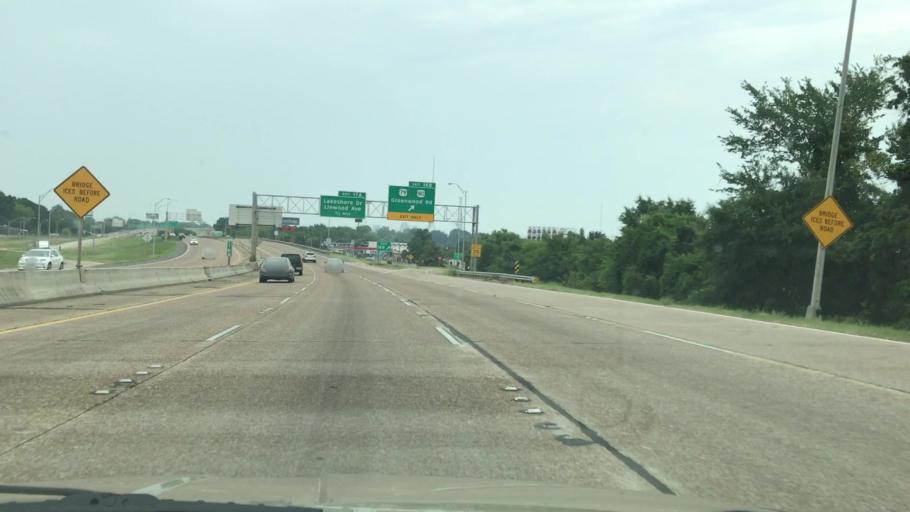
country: US
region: Louisiana
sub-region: Caddo Parish
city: Shreveport
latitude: 32.4828
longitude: -93.7754
